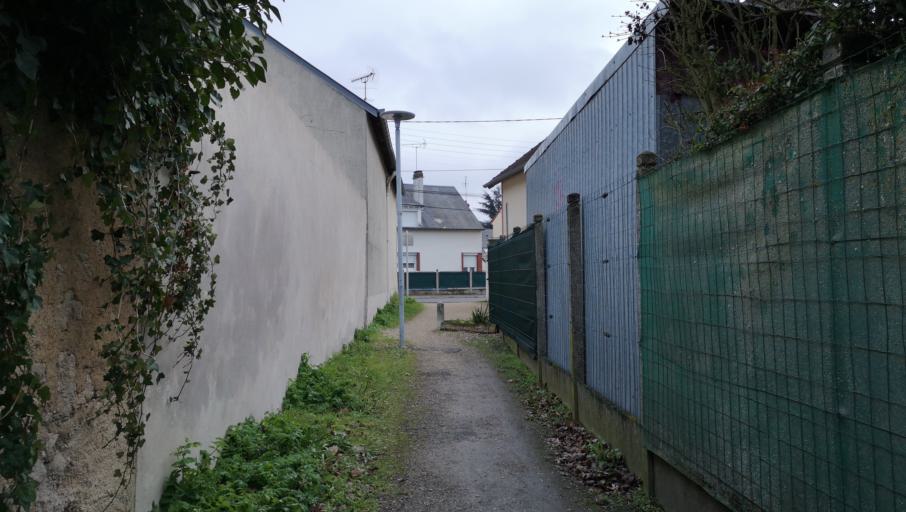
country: FR
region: Centre
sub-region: Departement du Loiret
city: Fleury-les-Aubrais
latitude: 47.9223
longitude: 1.9221
